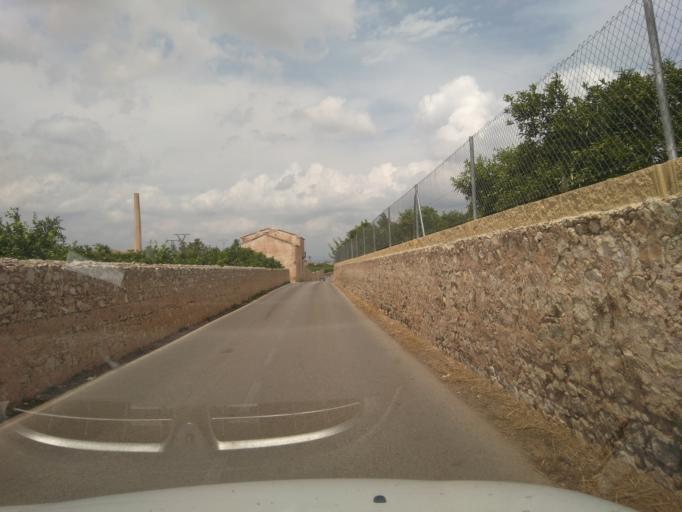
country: ES
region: Valencia
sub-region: Provincia de Valencia
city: Carcaixent
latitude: 39.1031
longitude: -0.4335
